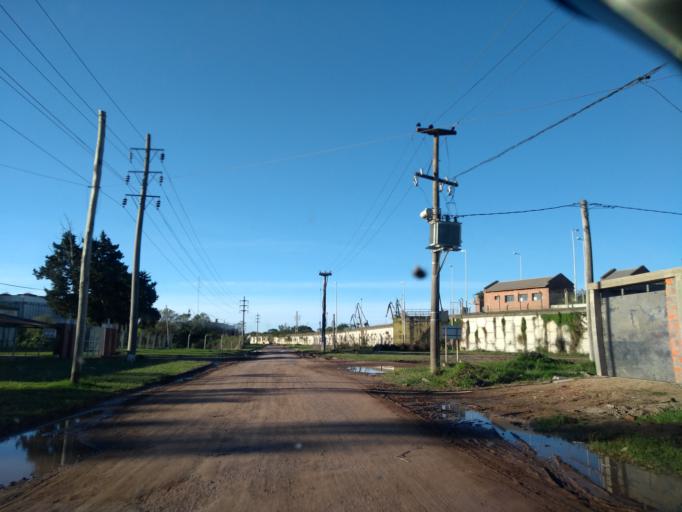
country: AR
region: Chaco
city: Barranqueras
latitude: -27.4942
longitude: -58.9292
